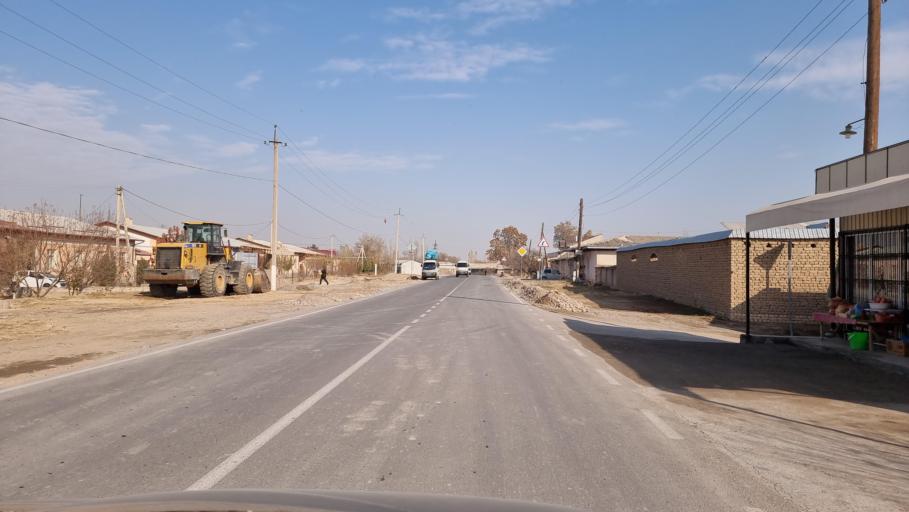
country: UZ
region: Toshkent
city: Urtaowul
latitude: 41.1887
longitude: 69.1223
